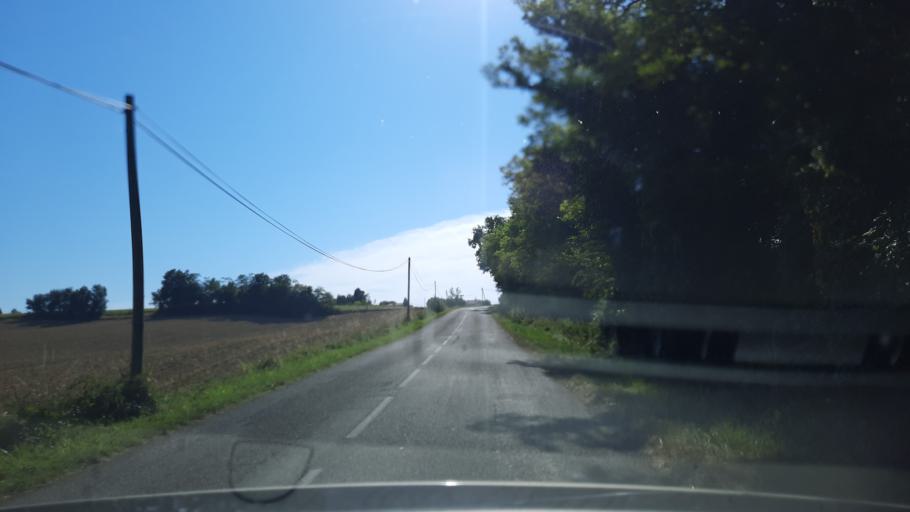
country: FR
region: Midi-Pyrenees
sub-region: Departement du Tarn-et-Garonne
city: Caussade
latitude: 44.1786
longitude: 1.4953
